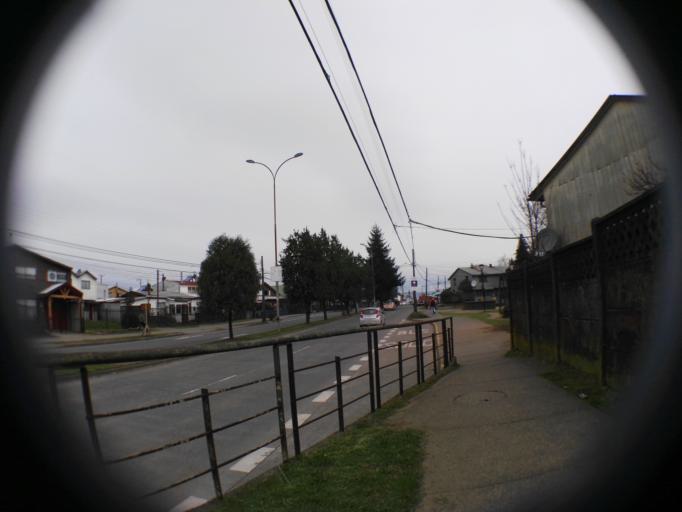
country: CL
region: Los Rios
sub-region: Provincia de Valdivia
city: Valdivia
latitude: -39.8285
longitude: -73.2353
